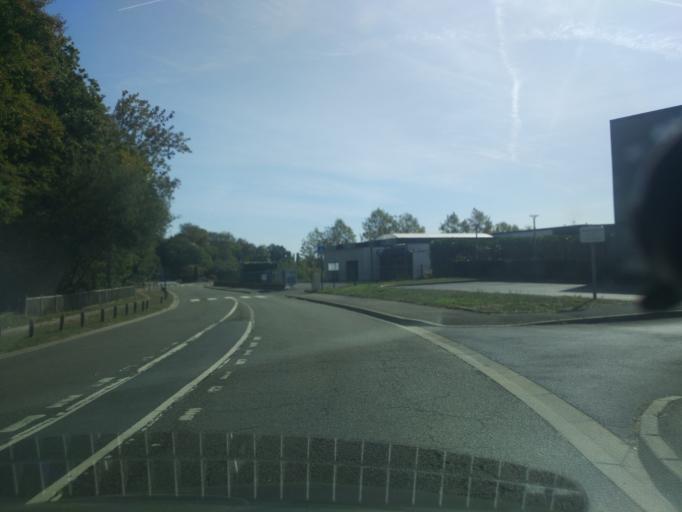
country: FR
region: Ile-de-France
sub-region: Departement de l'Essonne
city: Limours
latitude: 48.6448
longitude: 2.0904
